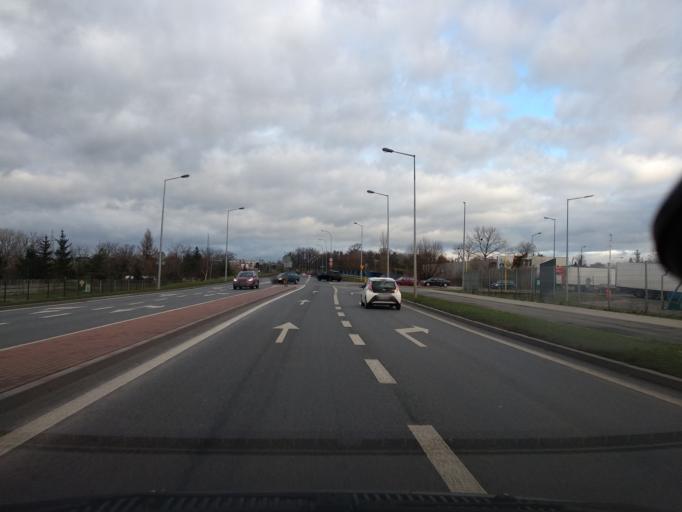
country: PL
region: Greater Poland Voivodeship
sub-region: Kalisz
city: Kalisz
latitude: 51.7713
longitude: 18.0723
